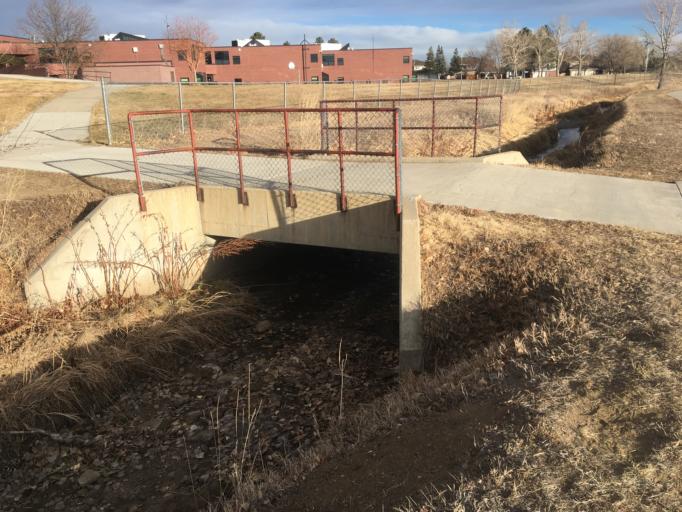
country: US
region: Colorado
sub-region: Broomfield County
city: Broomfield
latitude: 39.9373
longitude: -105.0794
